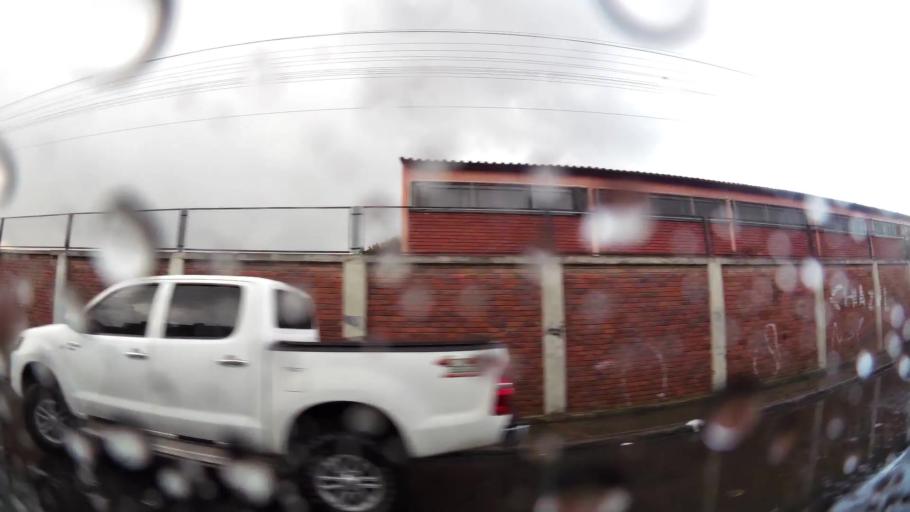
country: CO
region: Cundinamarca
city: Chia
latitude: 4.8565
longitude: -74.0617
